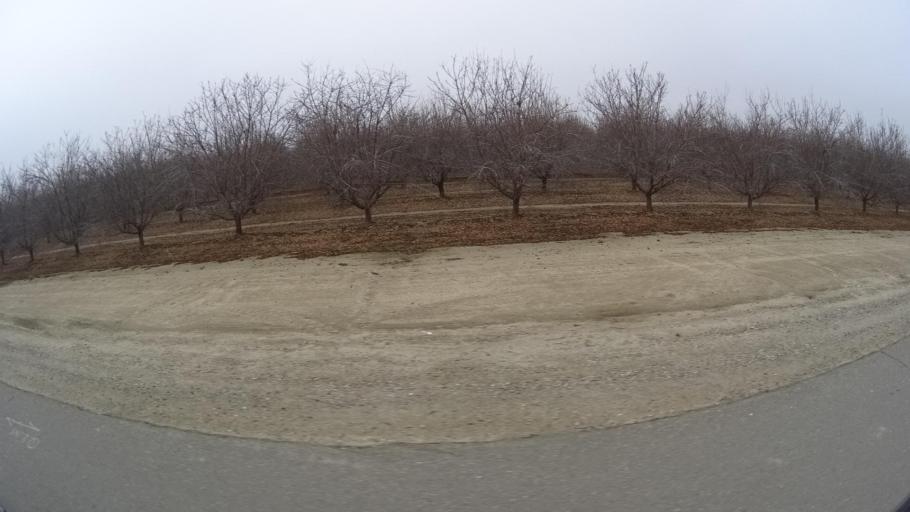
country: US
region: California
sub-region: Kern County
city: Greenfield
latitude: 35.2299
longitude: -119.1099
